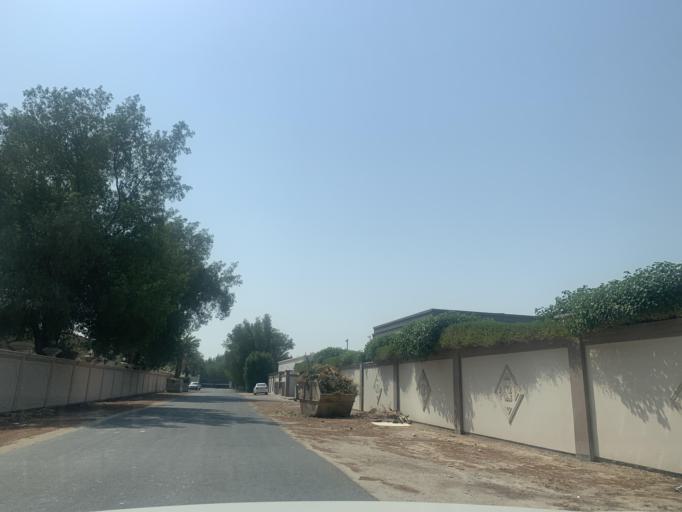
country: BH
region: Central Governorate
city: Madinat Hamad
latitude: 26.1704
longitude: 50.4604
